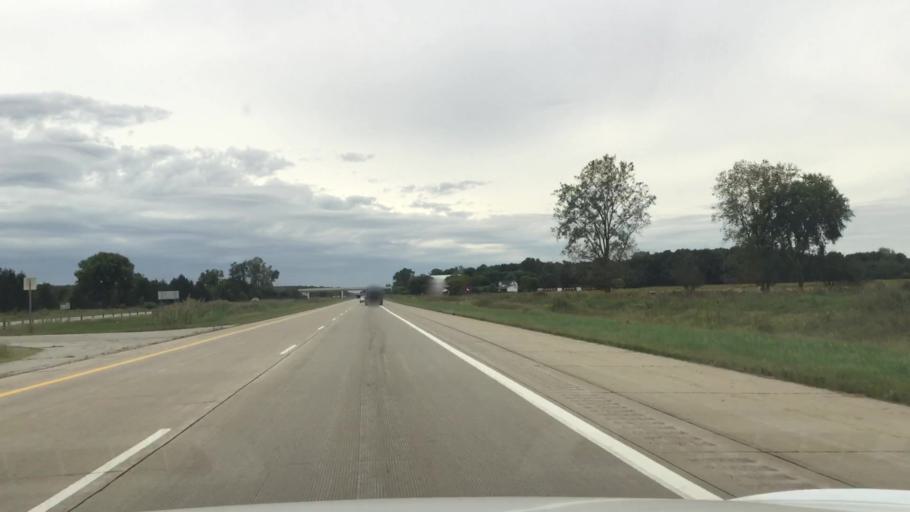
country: US
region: Michigan
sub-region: Saint Clair County
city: Saint Clair
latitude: 42.8554
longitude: -82.5677
